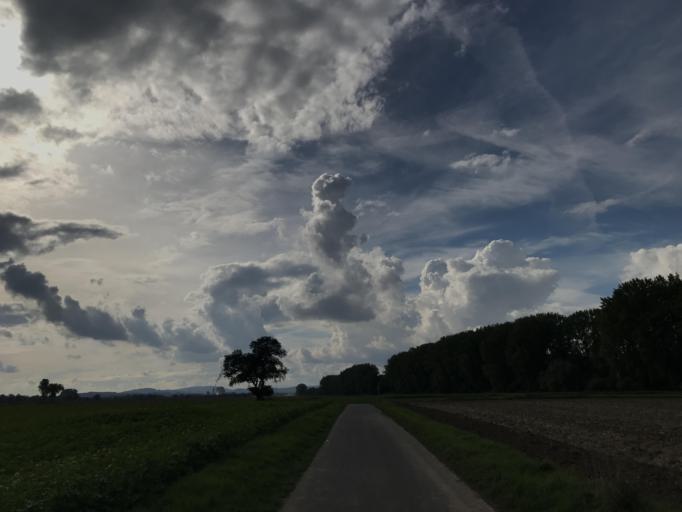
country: DE
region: Hesse
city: Felsberg
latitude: 51.1138
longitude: 9.3996
